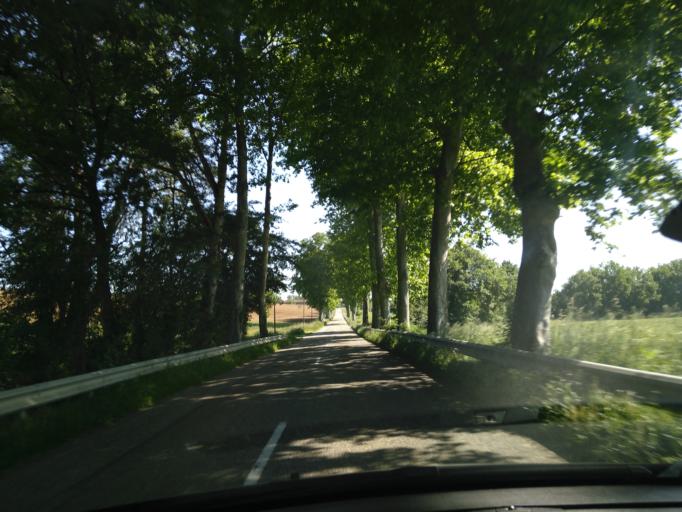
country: FR
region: Midi-Pyrenees
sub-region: Departement du Gers
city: Gimont
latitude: 43.5795
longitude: 0.8190
